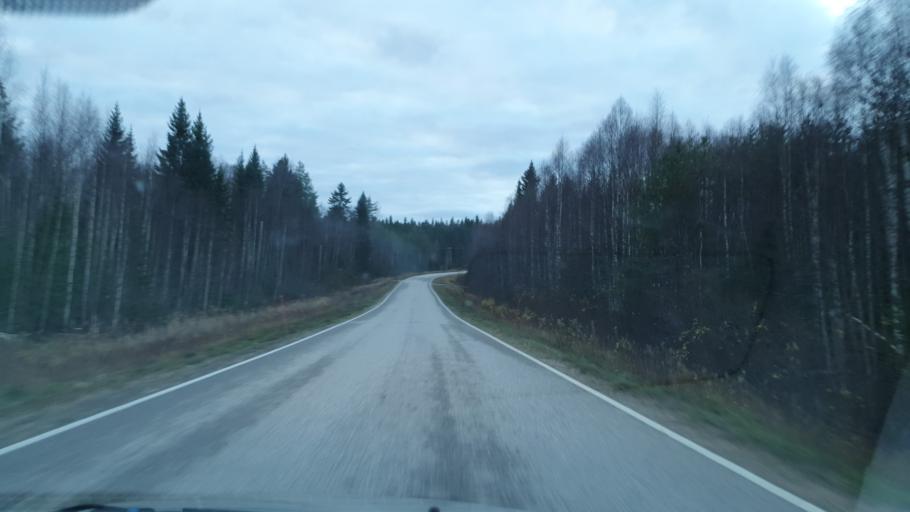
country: FI
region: Kainuu
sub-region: Kajaani
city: Ristijaervi
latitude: 64.4278
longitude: 28.3853
